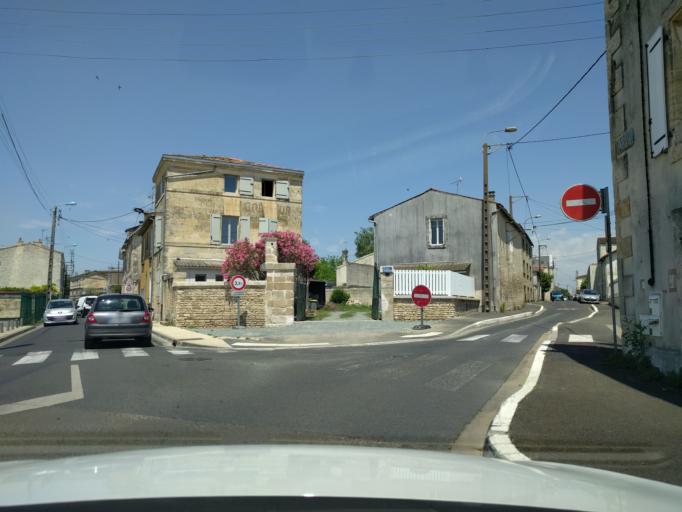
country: FR
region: Poitou-Charentes
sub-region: Departement des Deux-Sevres
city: Niort
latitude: 46.3315
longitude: -0.4596
